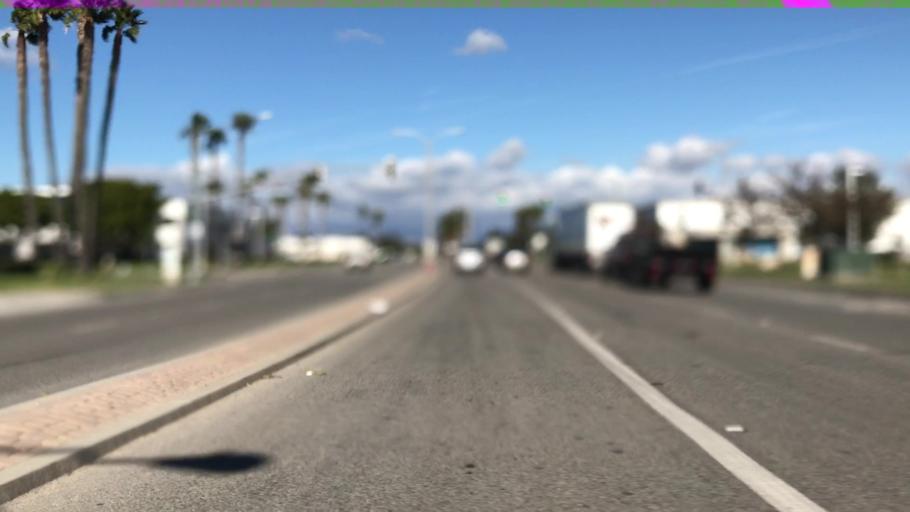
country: US
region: California
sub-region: Ventura County
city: El Rio
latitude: 34.2045
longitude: -119.1272
